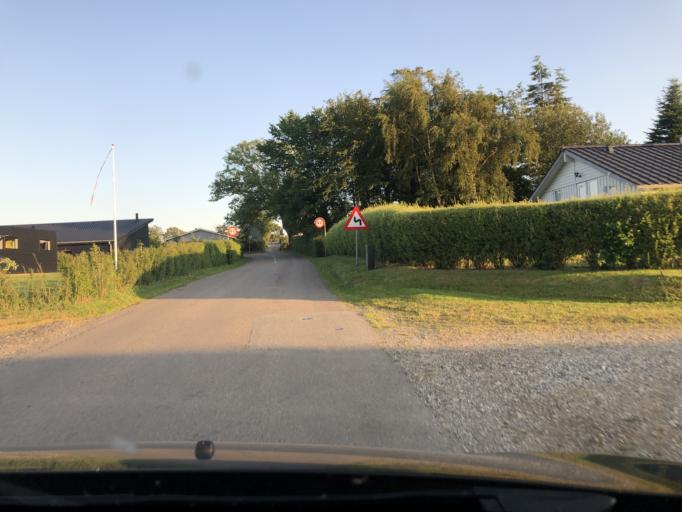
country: DK
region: South Denmark
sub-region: Vejle Kommune
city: Brejning
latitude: 55.6465
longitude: 9.7406
